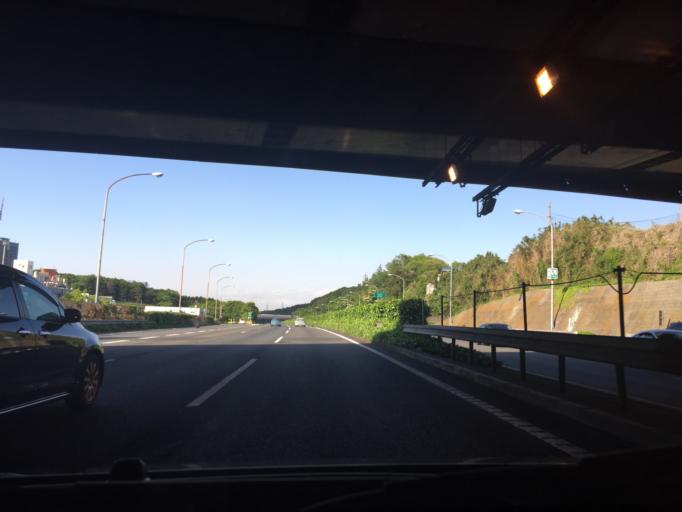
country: JP
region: Kanagawa
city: Minami-rinkan
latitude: 35.5054
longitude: 139.4821
